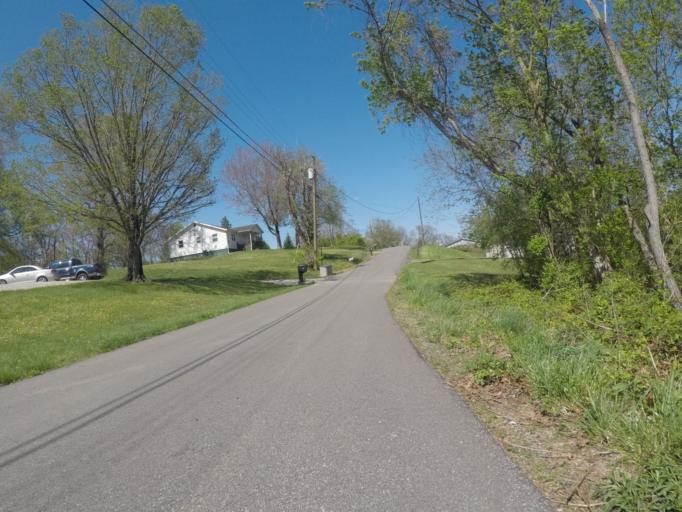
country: US
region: West Virginia
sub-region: Wayne County
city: Kenova
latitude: 38.3947
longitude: -82.5894
